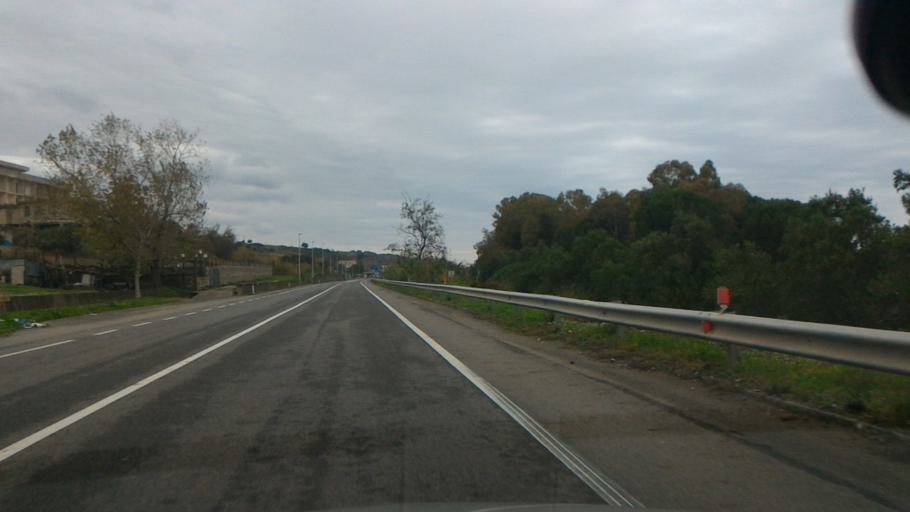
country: IT
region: Calabria
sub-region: Provincia di Crotone
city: Torretta
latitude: 39.4319
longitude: 17.0601
